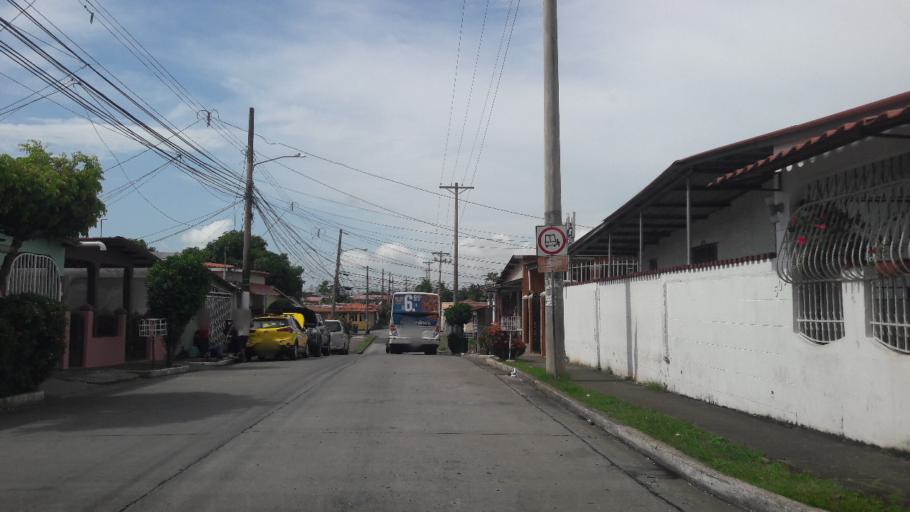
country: PA
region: Panama
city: Tocumen
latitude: 9.0545
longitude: -79.4179
